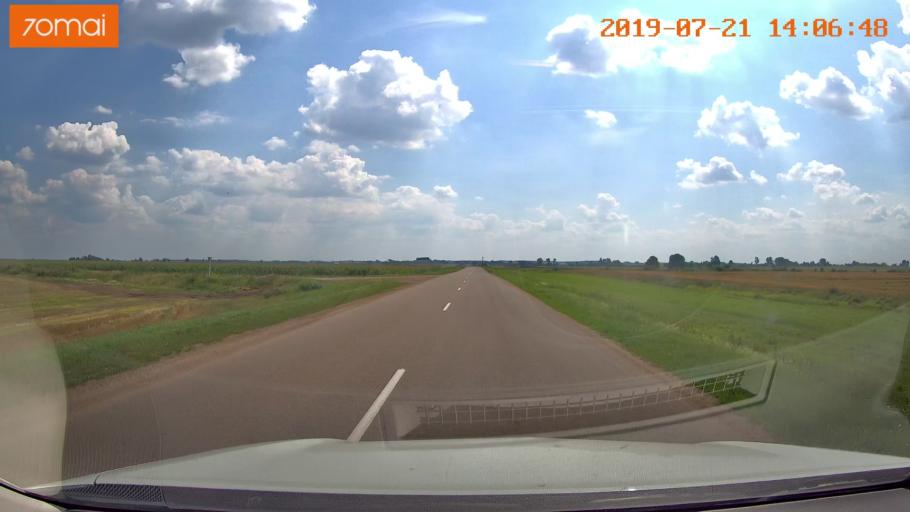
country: BY
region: Grodnenskaya
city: Lyubcha
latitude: 53.6920
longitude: 26.1144
